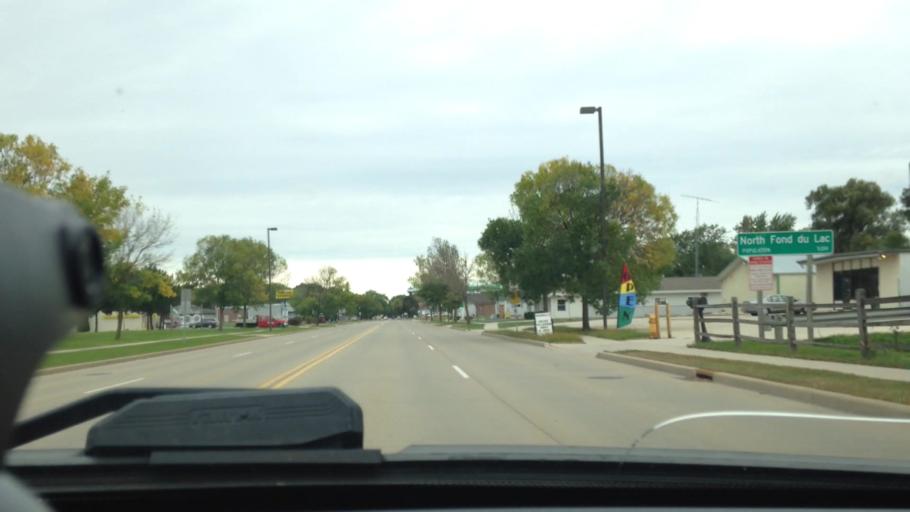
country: US
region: Wisconsin
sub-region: Fond du Lac County
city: North Fond du Lac
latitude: 43.8010
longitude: -88.4781
